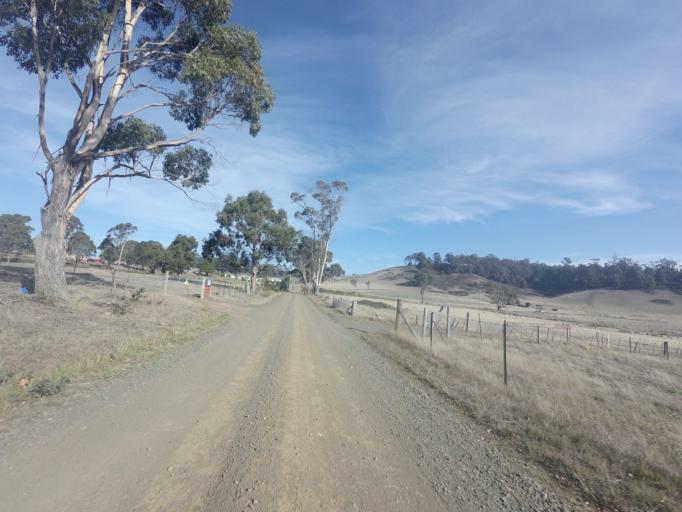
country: AU
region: Tasmania
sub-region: Sorell
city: Sorell
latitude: -42.4810
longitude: 147.4804
